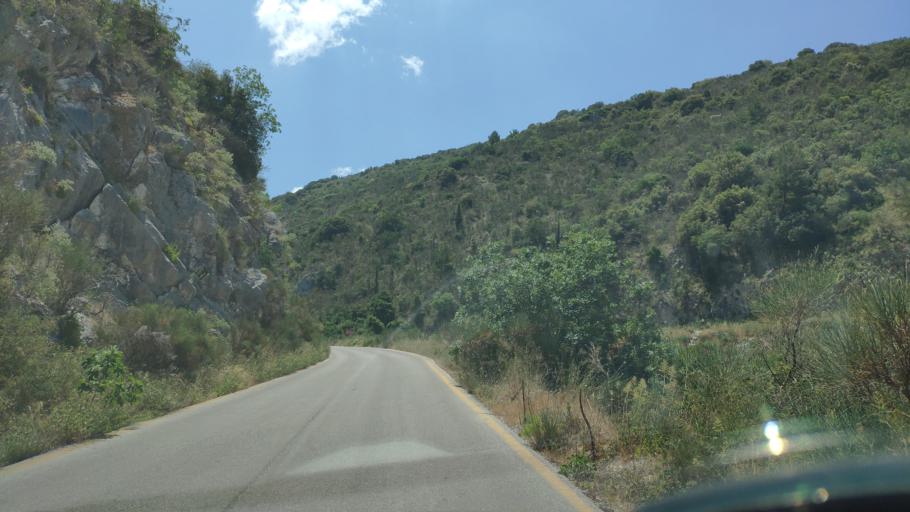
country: GR
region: Ionian Islands
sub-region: Lefkada
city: Nidri
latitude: 38.7448
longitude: 20.6215
